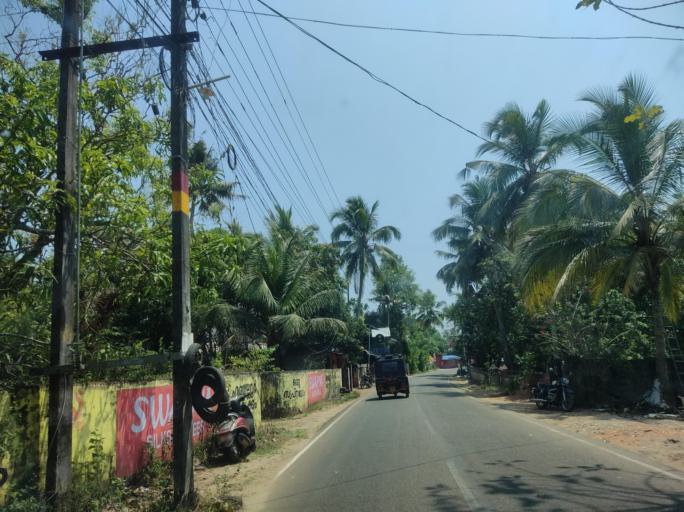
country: IN
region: Kerala
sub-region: Alappuzha
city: Kutiatodu
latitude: 9.8096
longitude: 76.3007
